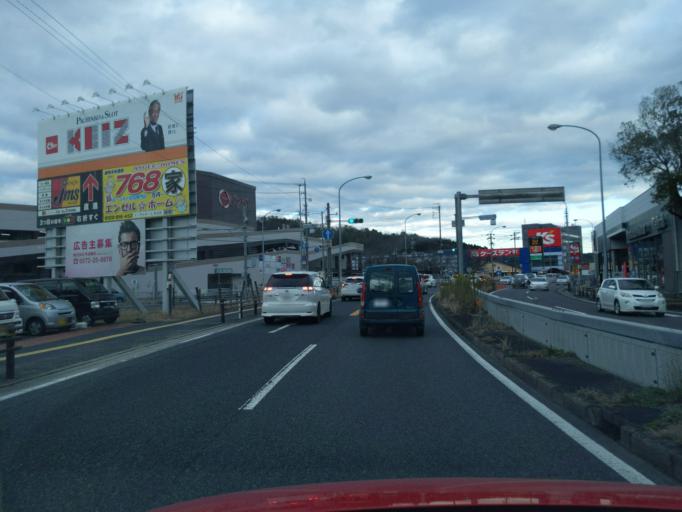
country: JP
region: Gifu
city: Tajimi
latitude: 35.3429
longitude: 137.1218
